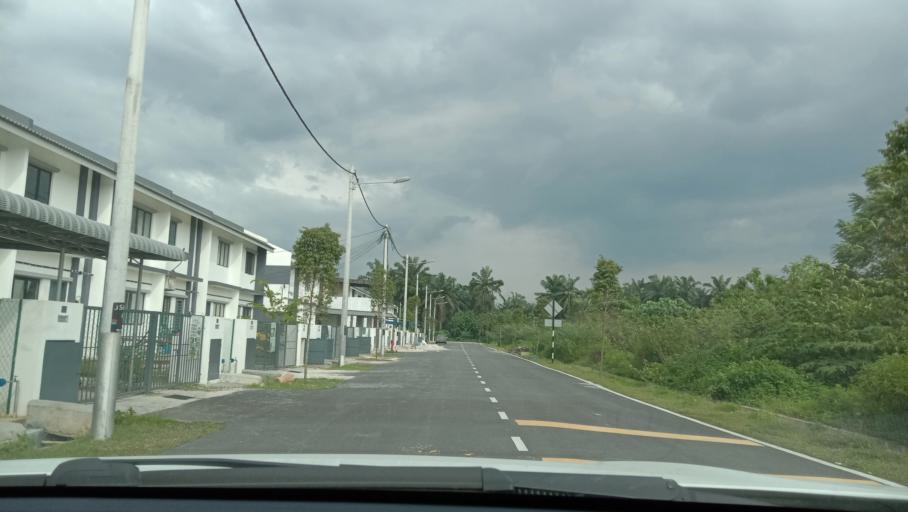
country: MY
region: Selangor
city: Ladang Seri Kundang
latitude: 3.2344
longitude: 101.4779
